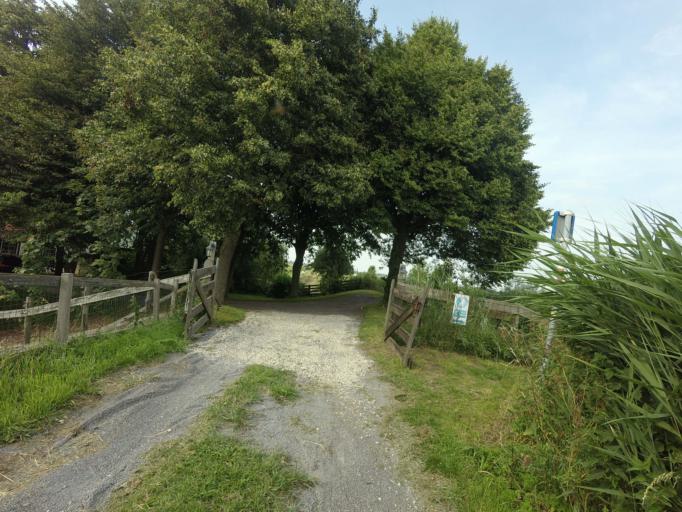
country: NL
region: South Holland
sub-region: Bodegraven-Reeuwijk
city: Bodegraven
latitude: 52.0505
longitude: 4.7786
